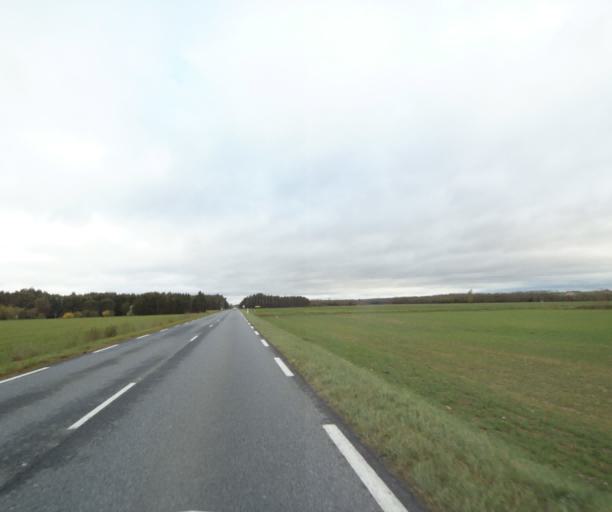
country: FR
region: Midi-Pyrenees
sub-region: Departement de l'Ariege
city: Saverdun
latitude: 43.2698
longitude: 1.5522
